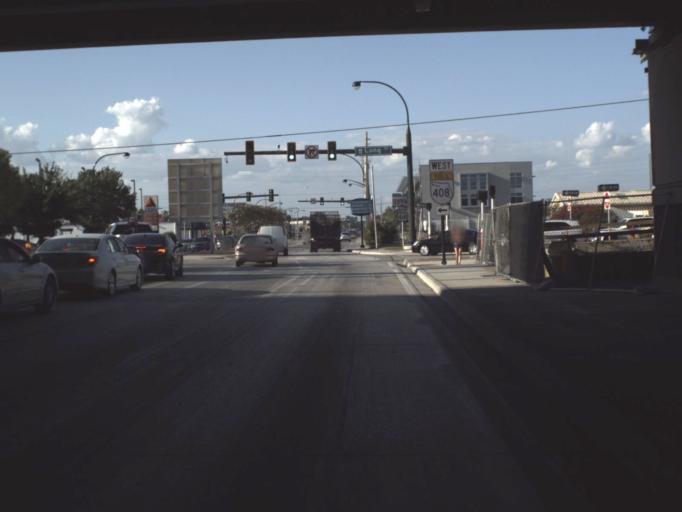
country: US
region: Florida
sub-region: Orange County
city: Orlando
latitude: 28.5352
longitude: -81.3971
